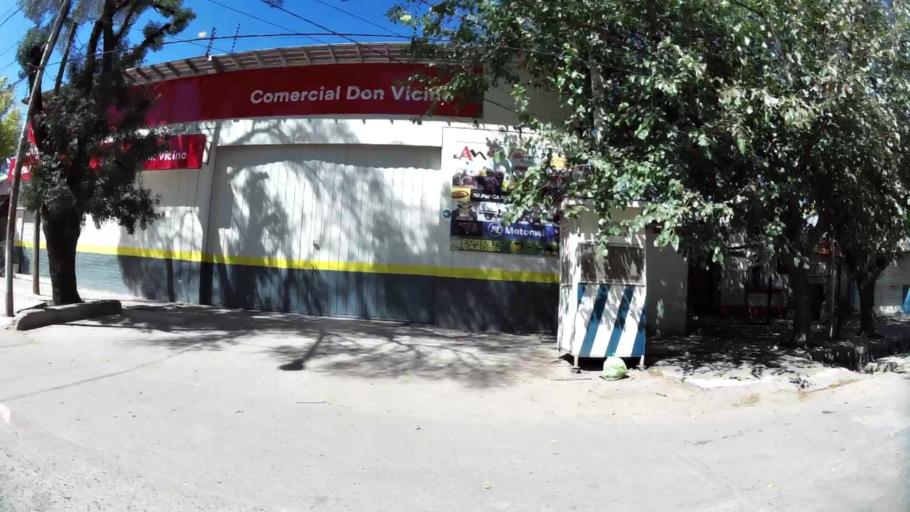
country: AR
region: Mendoza
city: Las Heras
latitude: -32.8508
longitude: -68.8343
